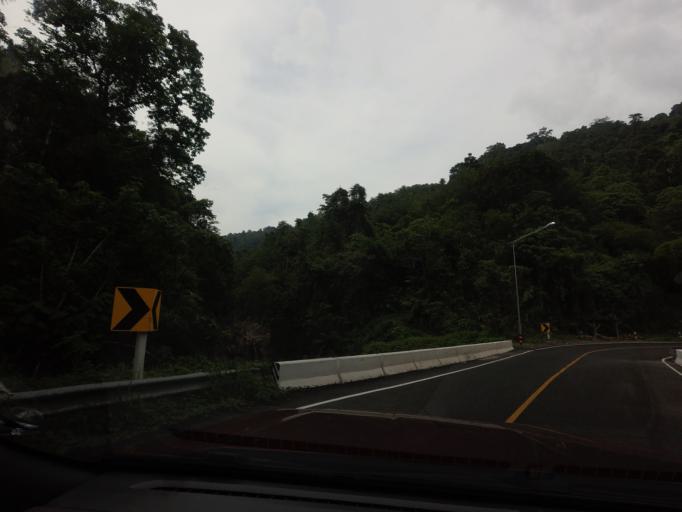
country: TH
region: Yala
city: Than To
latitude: 6.1365
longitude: 101.3019
